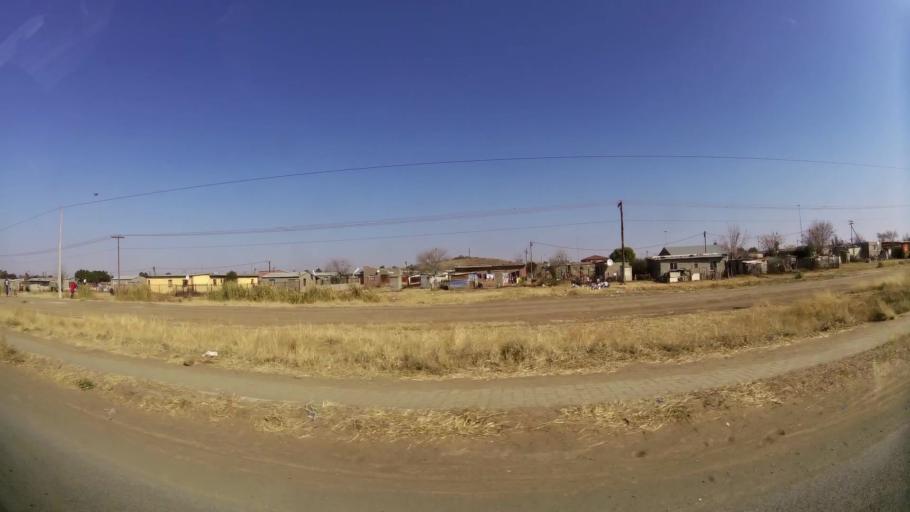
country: ZA
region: Orange Free State
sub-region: Mangaung Metropolitan Municipality
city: Bloemfontein
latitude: -29.1671
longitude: 26.2596
